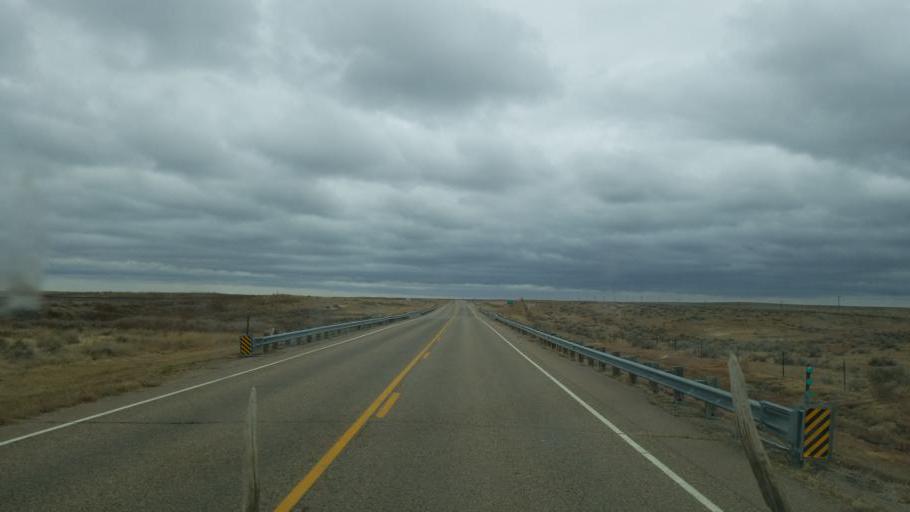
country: US
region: Colorado
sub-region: Kiowa County
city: Eads
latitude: 38.7885
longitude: -102.6829
